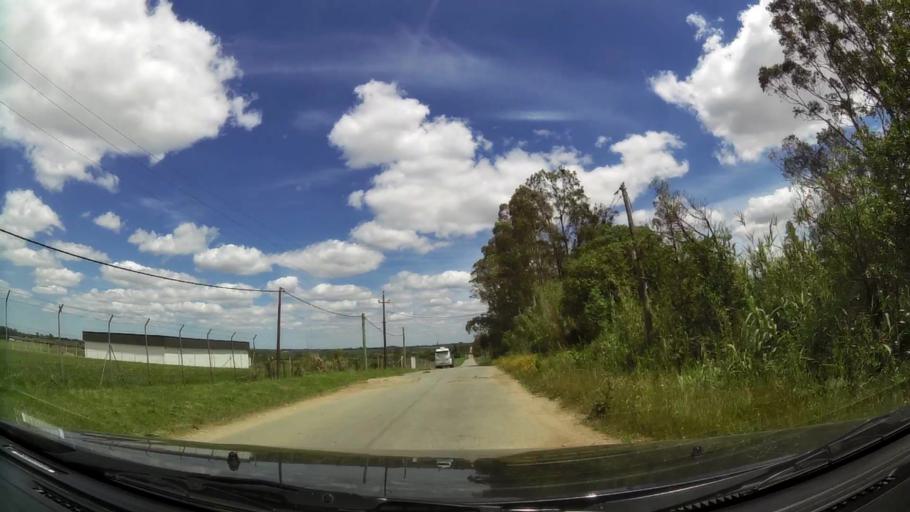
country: UY
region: Canelones
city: Colonia Nicolich
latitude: -34.7995
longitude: -56.0090
